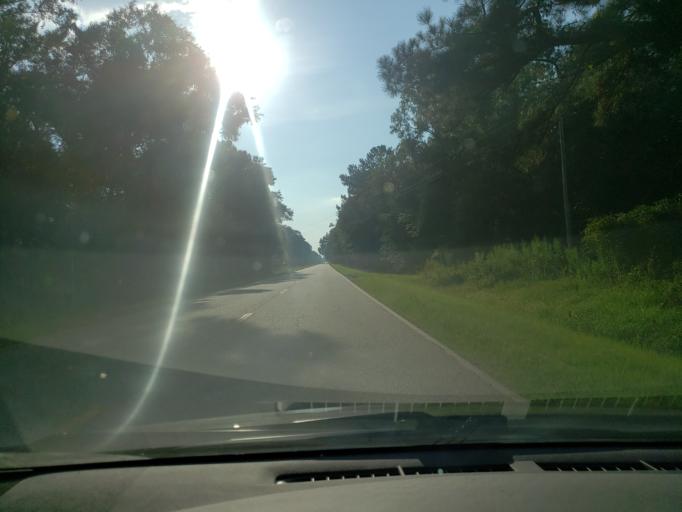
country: US
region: Georgia
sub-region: Dougherty County
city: Albany
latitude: 31.5733
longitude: -84.3362
